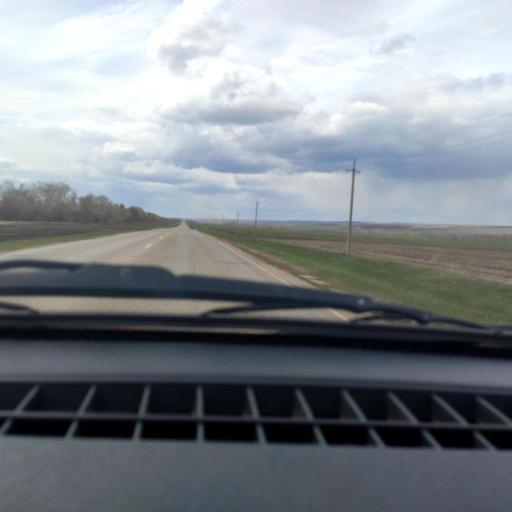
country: RU
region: Bashkortostan
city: Chekmagush
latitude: 55.1075
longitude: 54.9757
